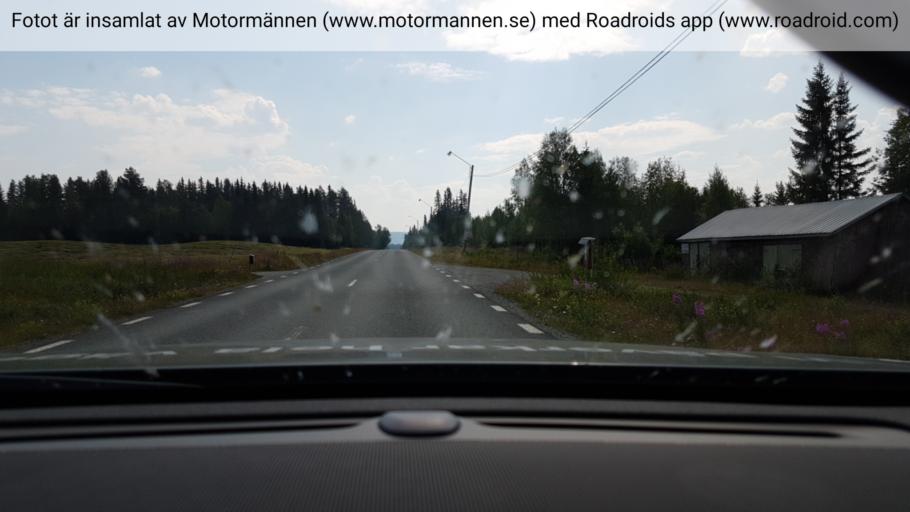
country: SE
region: Vaesterbotten
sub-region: Vilhelmina Kommun
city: Sjoberg
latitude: 65.4643
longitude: 16.0784
